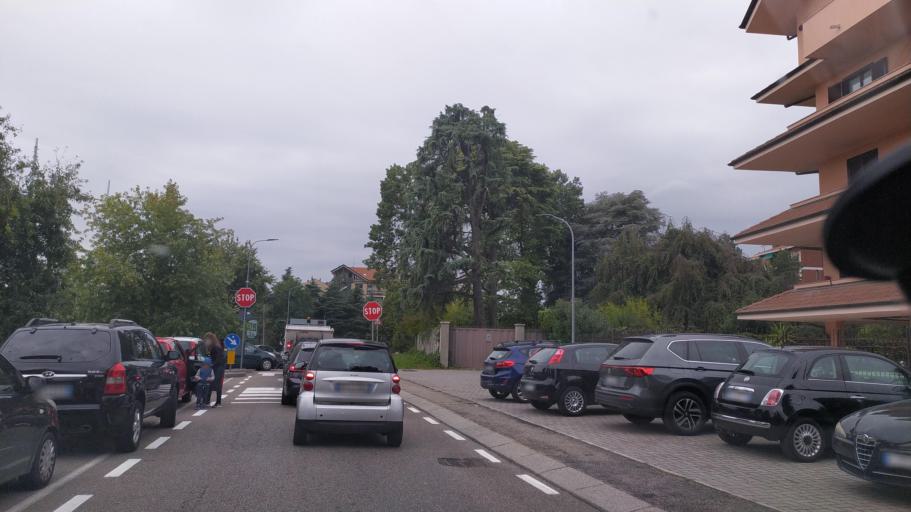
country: IT
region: Lombardy
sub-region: Provincia di Monza e Brianza
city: Seregno
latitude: 45.6449
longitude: 9.2100
